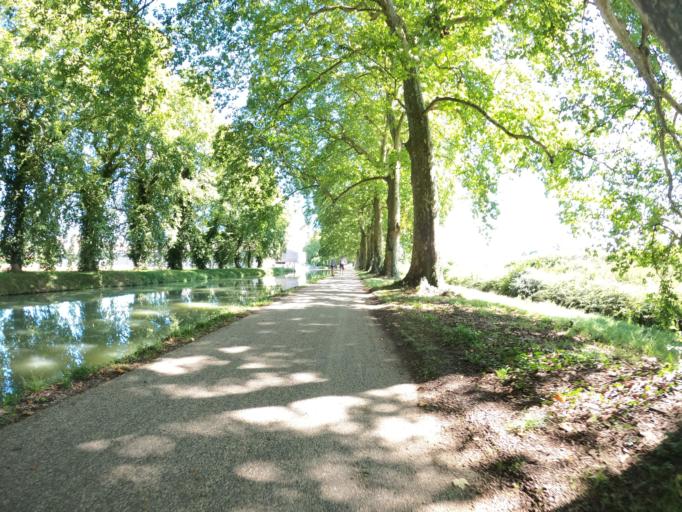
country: FR
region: Midi-Pyrenees
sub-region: Departement du Tarn-et-Garonne
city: Auvillar
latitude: 44.0903
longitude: 0.9619
